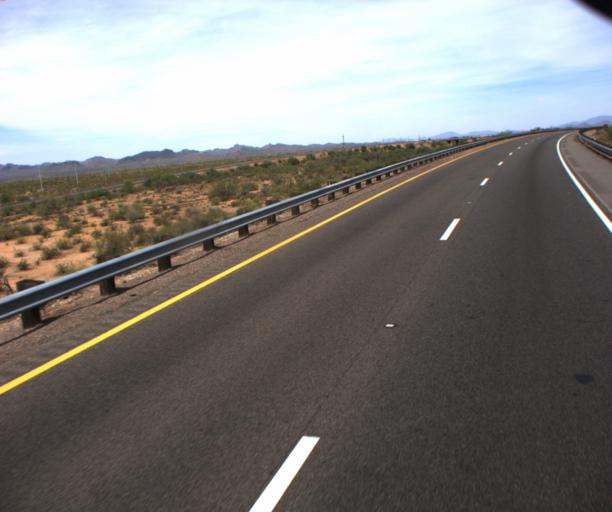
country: US
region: Arizona
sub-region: Maricopa County
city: Wickenburg
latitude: 33.8402
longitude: -112.6099
